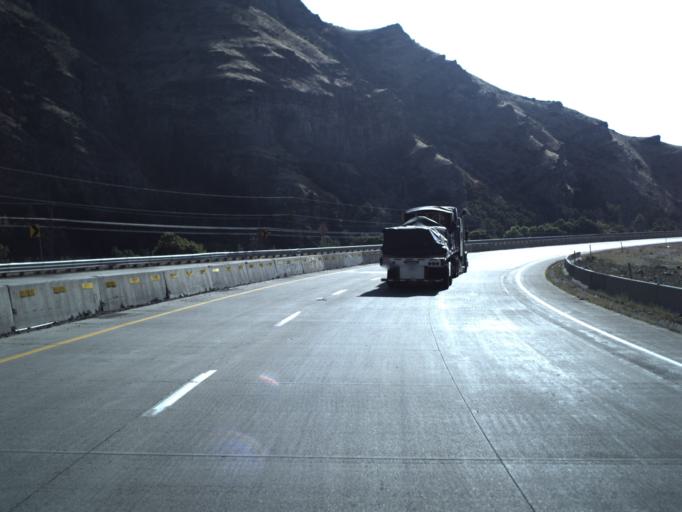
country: US
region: Utah
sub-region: Morgan County
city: Morgan
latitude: 41.0538
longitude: -111.5940
